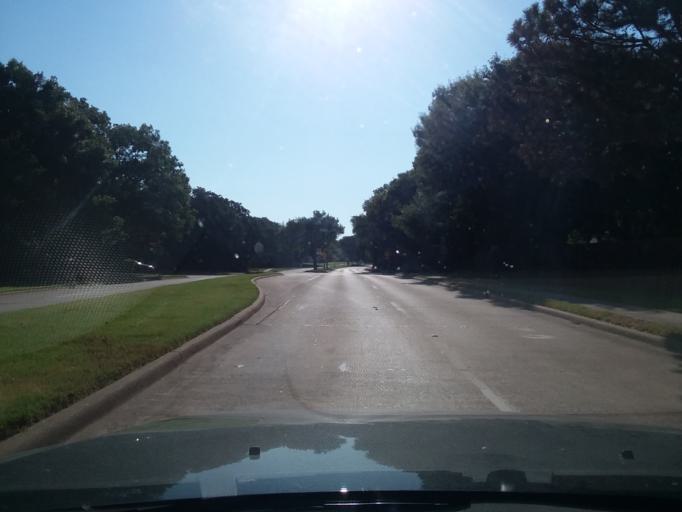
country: US
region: Texas
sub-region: Denton County
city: Highland Village
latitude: 33.0521
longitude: -97.0607
